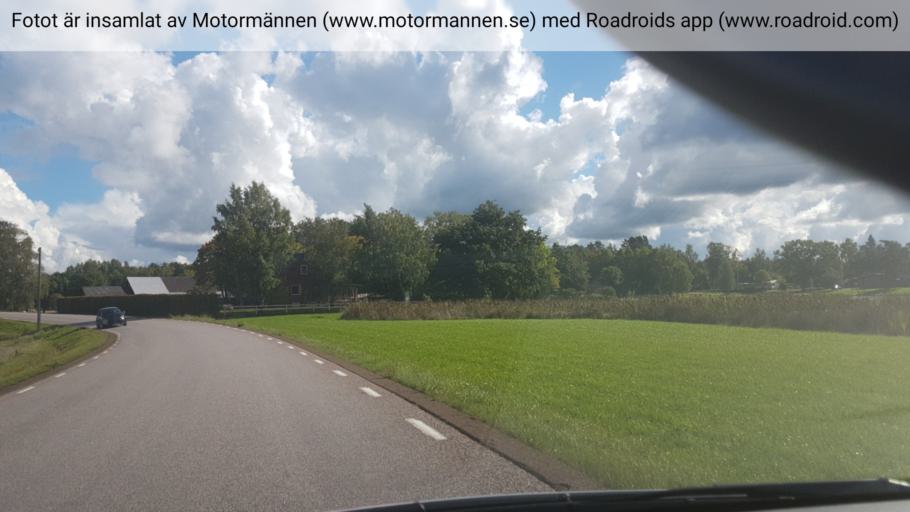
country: SE
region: Vaestra Goetaland
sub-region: Gotene Kommun
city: Goetene
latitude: 58.5321
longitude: 13.5302
